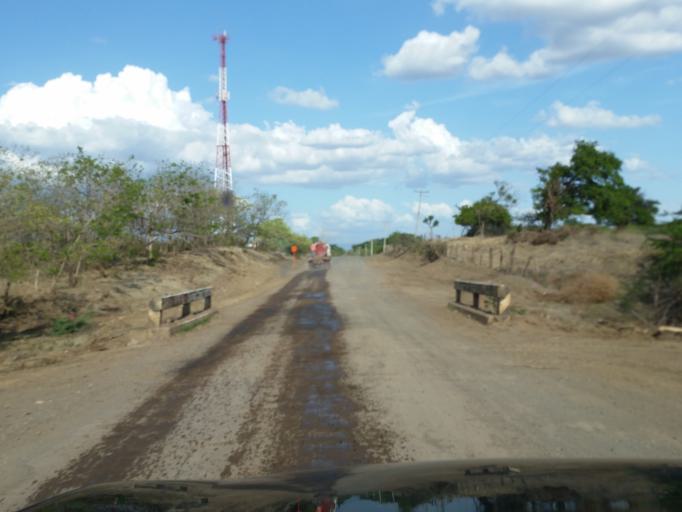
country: NI
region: Leon
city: Nagarote
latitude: 12.1120
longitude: -86.6026
